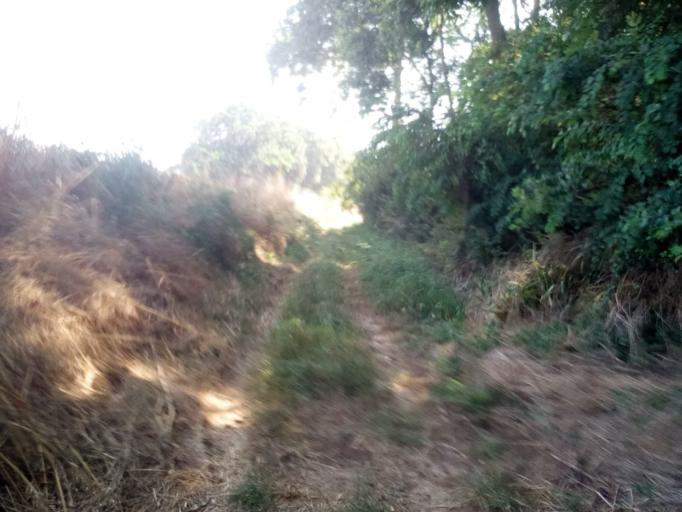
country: FR
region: Lower Normandy
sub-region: Departement du Calvados
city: Bernieres-sur-Mer
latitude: 49.3074
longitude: -0.4245
